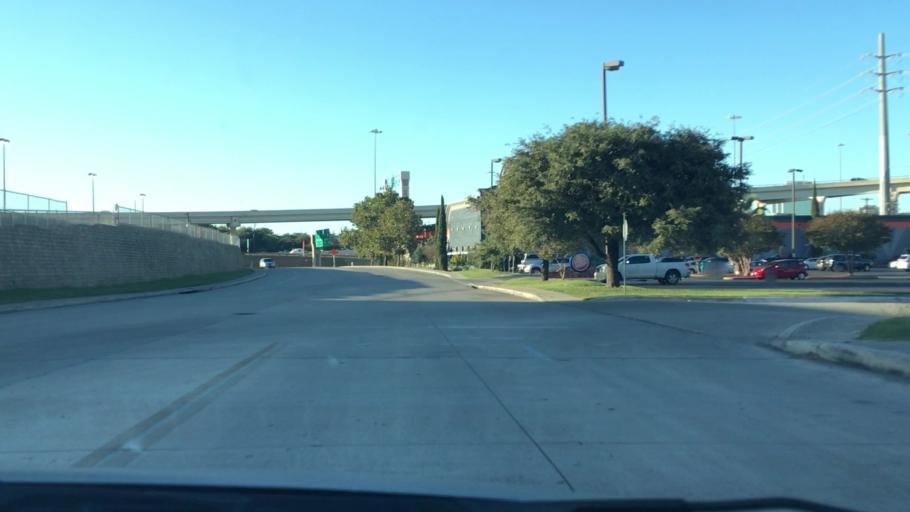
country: US
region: Texas
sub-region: Bexar County
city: Balcones Heights
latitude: 29.4949
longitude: -98.5498
